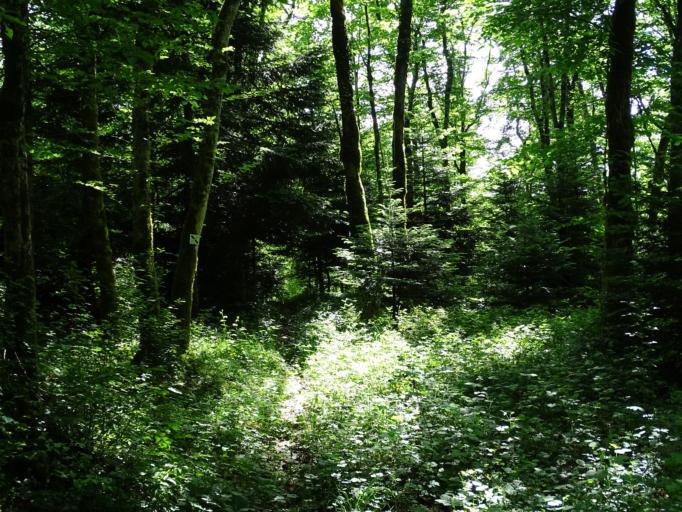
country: FR
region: Franche-Comte
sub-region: Departement du Doubs
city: Quingey
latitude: 47.0237
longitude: 5.9931
